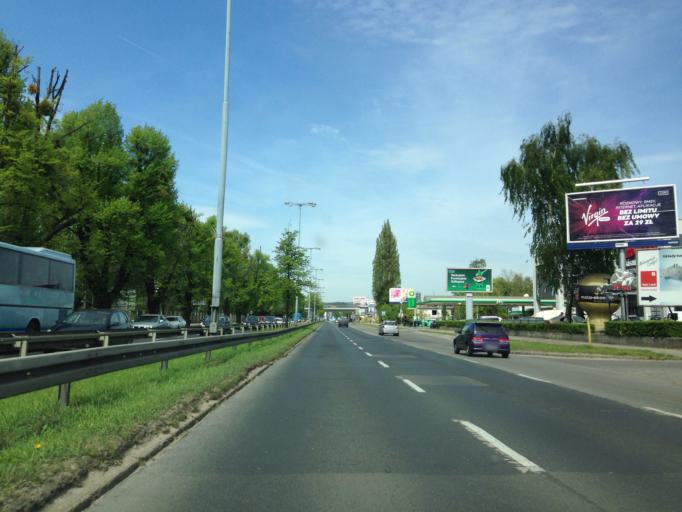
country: PL
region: Pomeranian Voivodeship
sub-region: Sopot
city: Sopot
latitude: 54.3898
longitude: 18.5875
